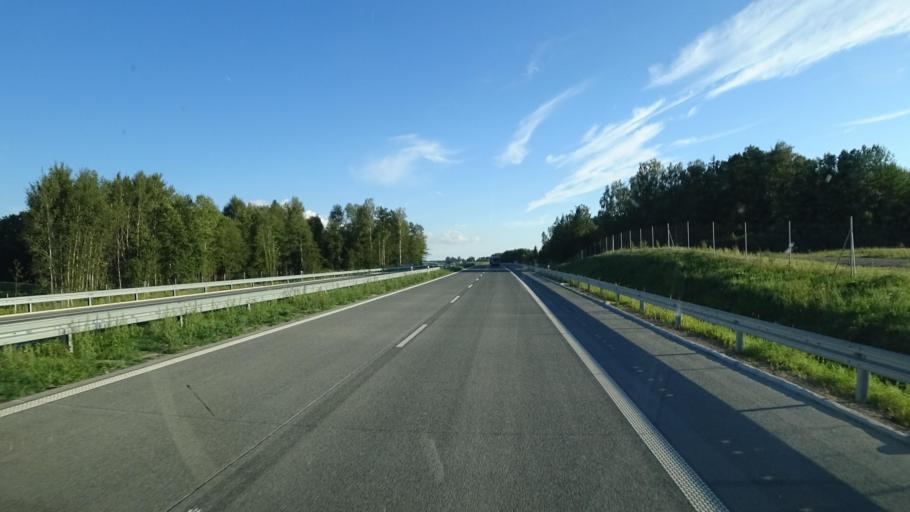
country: PL
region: Podlasie
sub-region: Powiat suwalski
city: Raczki
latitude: 53.9573
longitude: 22.7706
